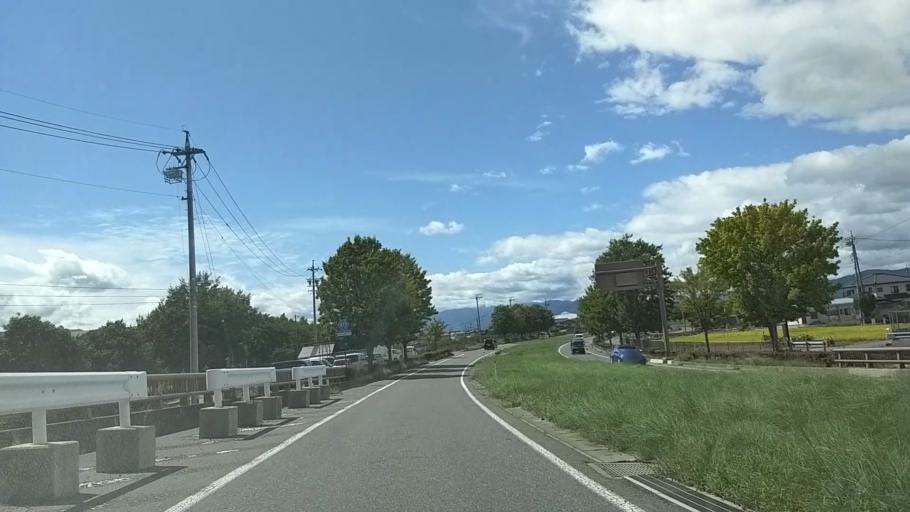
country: JP
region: Nagano
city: Nagano-shi
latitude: 36.6123
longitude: 138.2215
